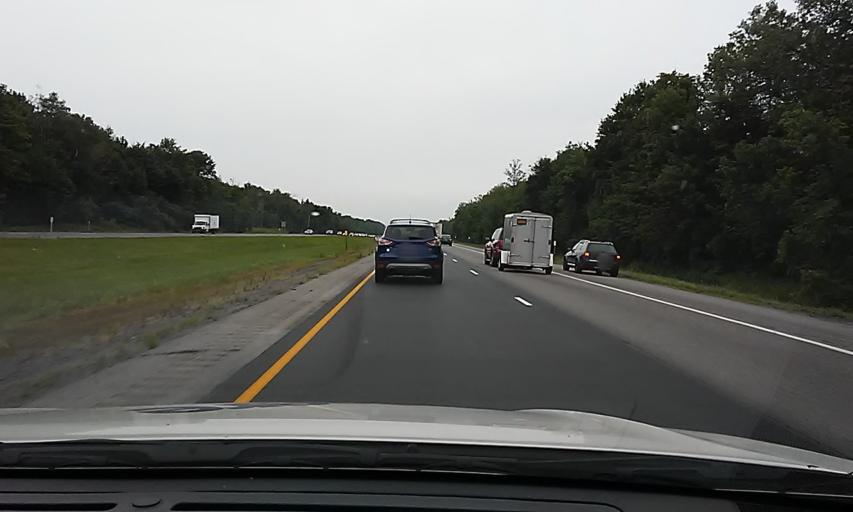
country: US
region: New York
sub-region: Erie County
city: Akron
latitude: 42.9886
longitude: -78.4520
